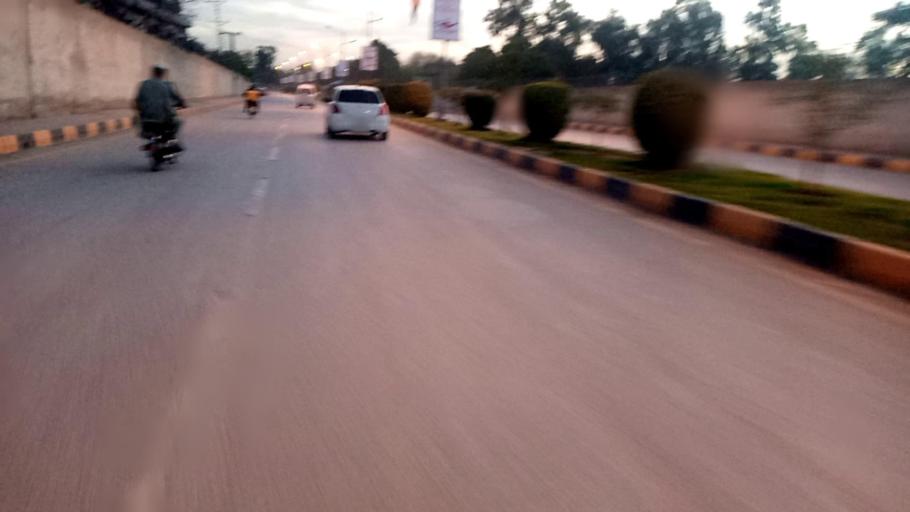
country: PK
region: Khyber Pakhtunkhwa
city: Peshawar
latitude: 34.0198
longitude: 71.5499
